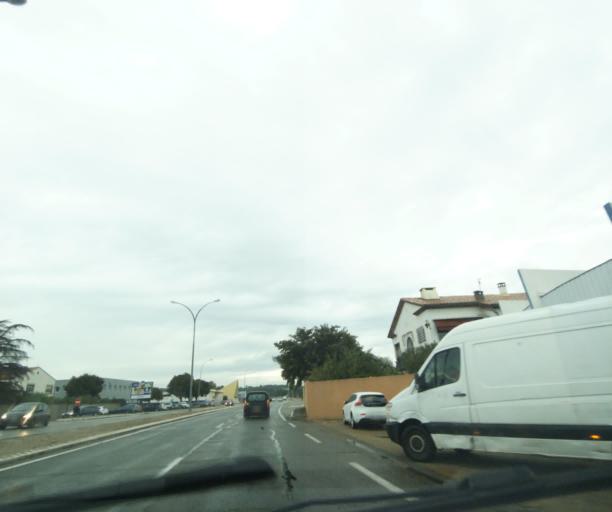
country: FR
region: Languedoc-Roussillon
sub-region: Departement du Gard
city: Rodilhan
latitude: 43.8534
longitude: 4.4011
